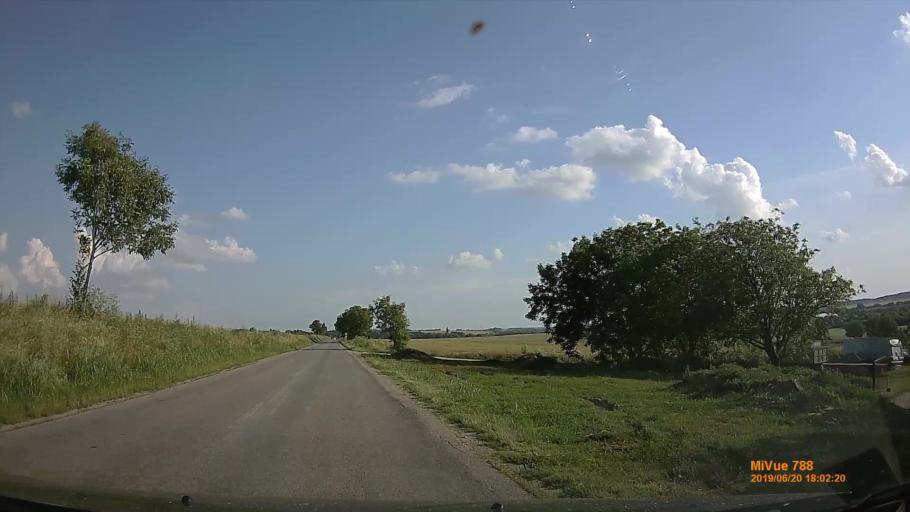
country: HU
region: Baranya
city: Buekkoesd
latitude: 46.0756
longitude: 17.9906
